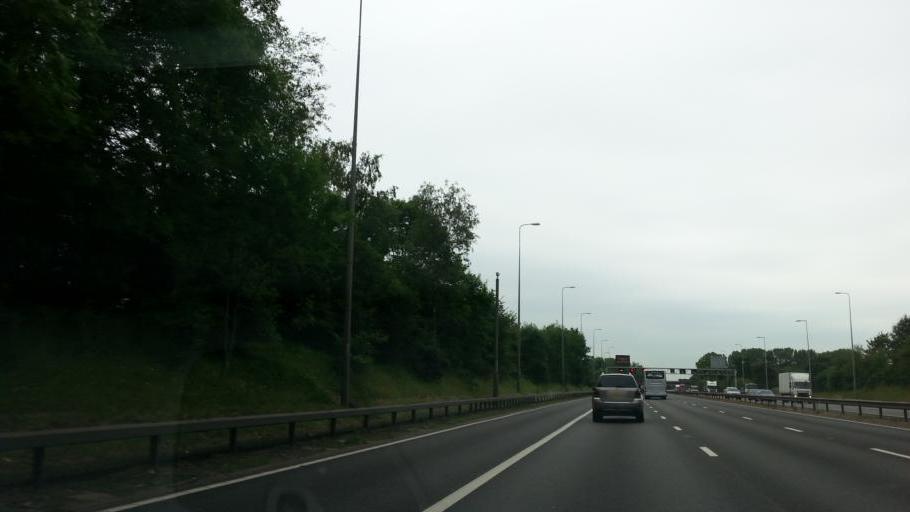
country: GB
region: England
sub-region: Solihull
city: Bickenhill
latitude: 52.4284
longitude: -1.7177
